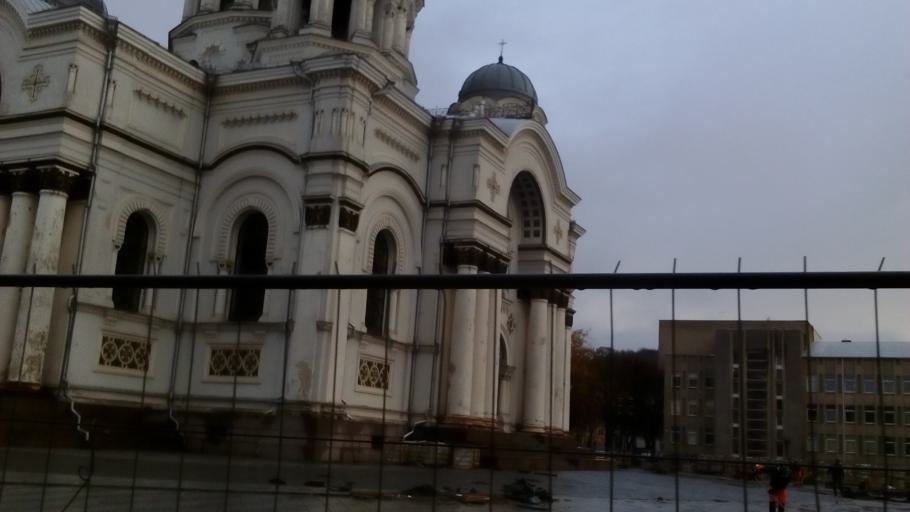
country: LT
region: Kauno apskritis
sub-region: Kaunas
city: Kaunas
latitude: 54.8969
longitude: 23.9172
